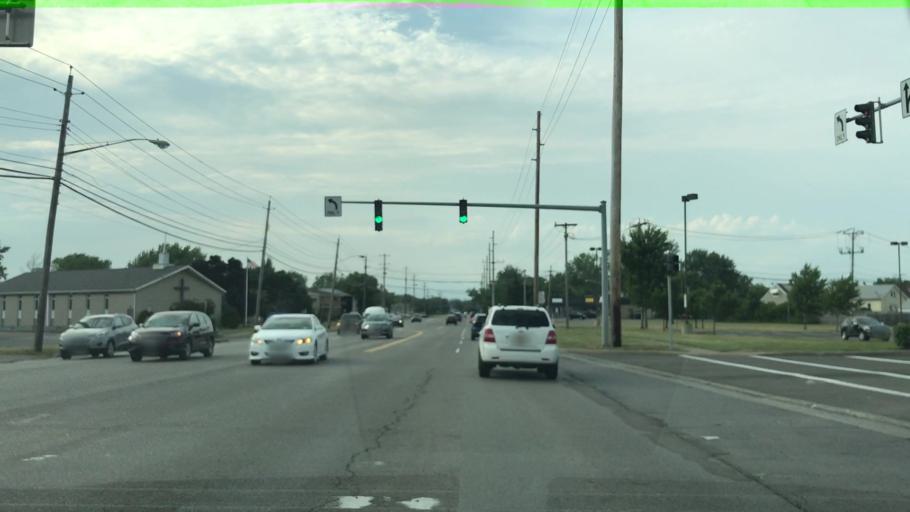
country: US
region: New York
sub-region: Erie County
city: Cheektowaga
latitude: 42.9201
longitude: -78.7384
